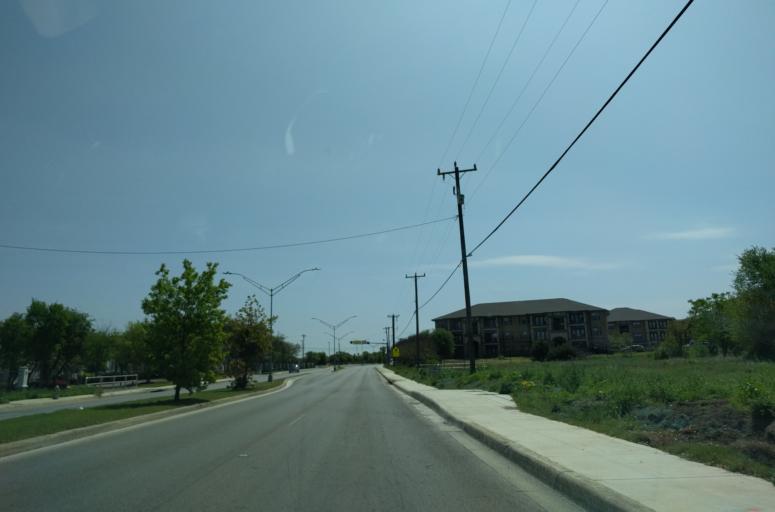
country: US
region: Texas
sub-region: Bexar County
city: Shavano Park
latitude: 29.5785
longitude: -98.5872
